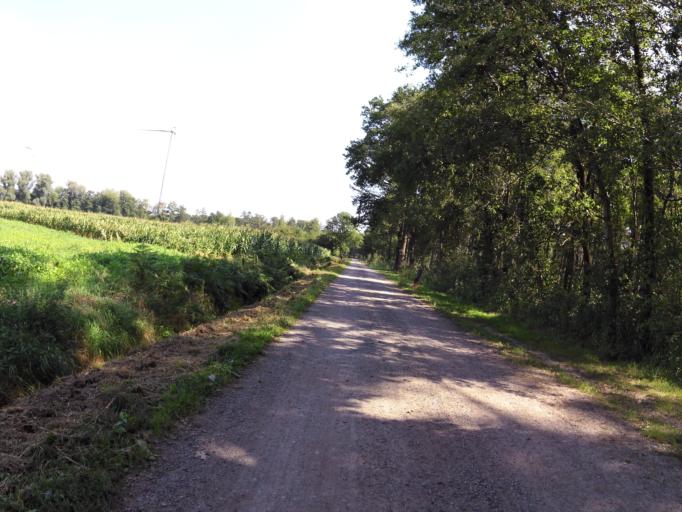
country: DE
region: North Rhine-Westphalia
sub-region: Regierungsbezirk Munster
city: Ahaus
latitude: 52.0228
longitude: 6.9907
